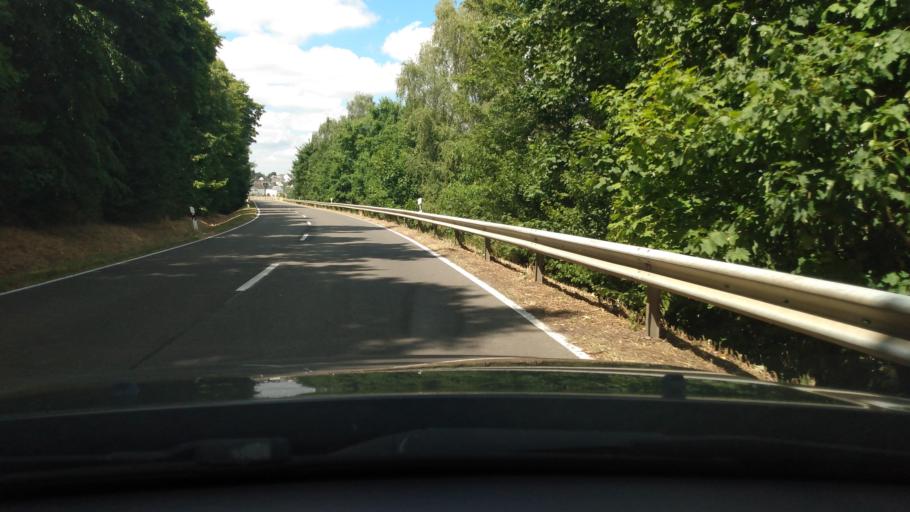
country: DE
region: Rheinland-Pfalz
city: Monzelfeld
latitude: 49.8884
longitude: 7.0838
